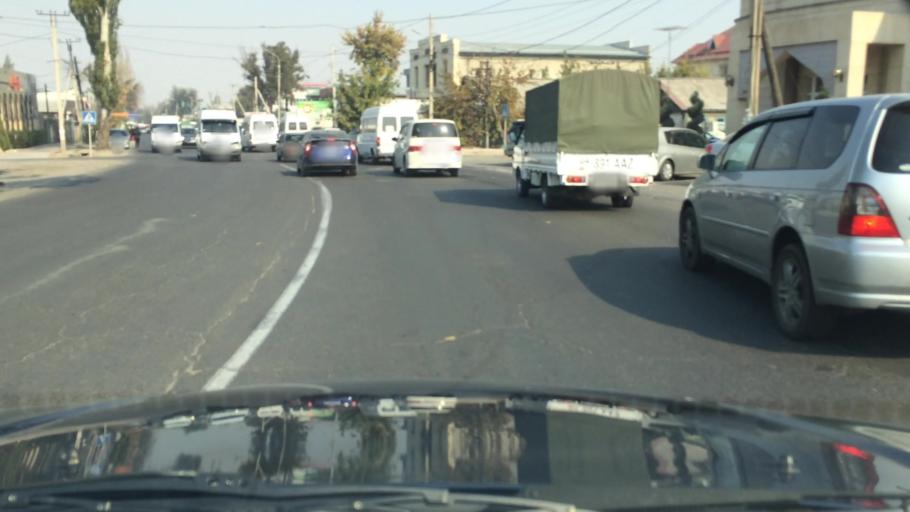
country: KG
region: Chuy
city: Lebedinovka
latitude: 42.8777
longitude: 74.6377
